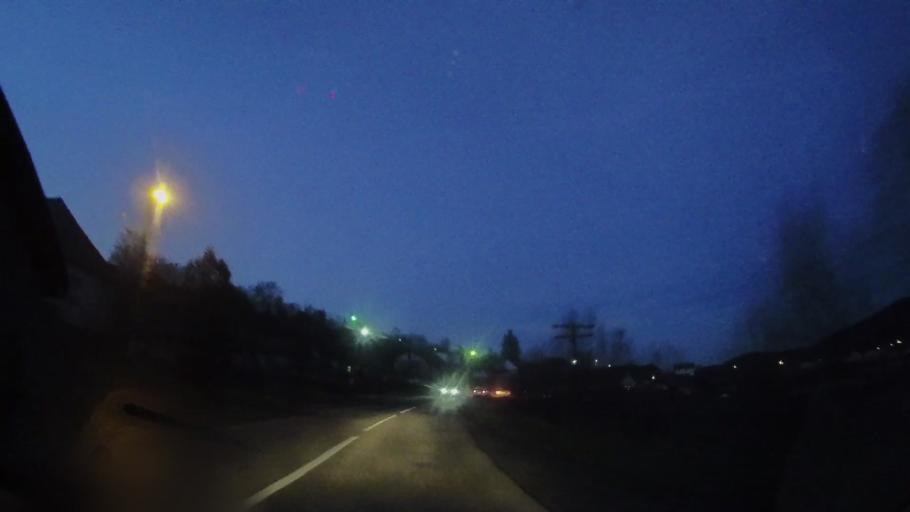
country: RO
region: Mures
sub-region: Comuna Sarmasu
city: Sarmasu
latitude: 46.7809
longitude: 24.2025
